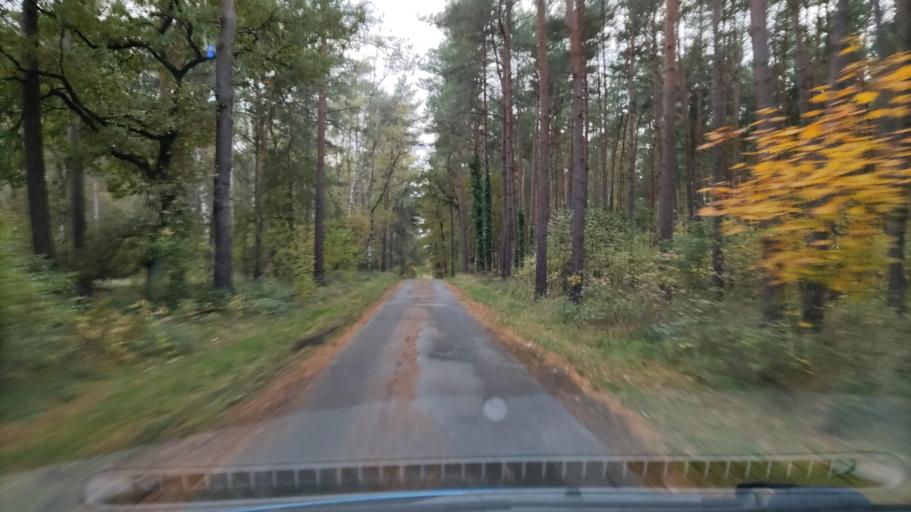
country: DE
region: Lower Saxony
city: Hitzacker
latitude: 53.1304
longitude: 11.0035
